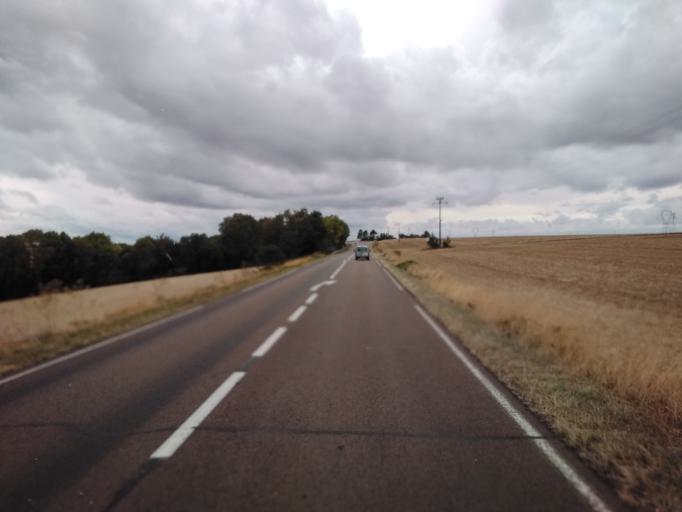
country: FR
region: Champagne-Ardenne
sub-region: Departement de la Marne
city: Frignicourt
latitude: 48.6118
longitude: 4.5603
